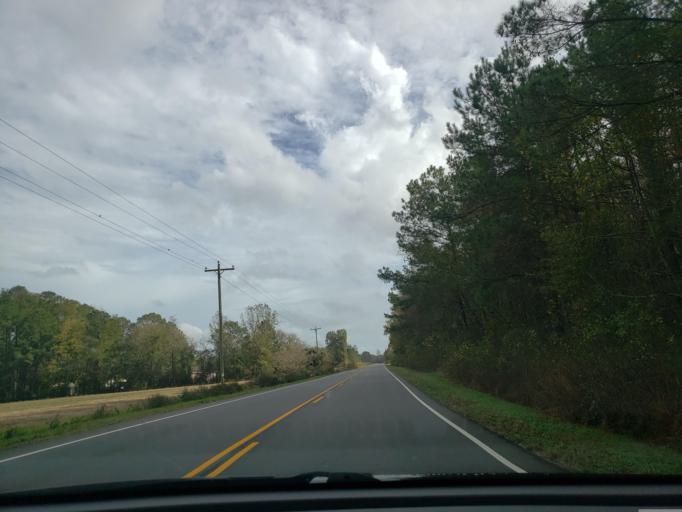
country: US
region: North Carolina
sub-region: Duplin County
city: Beulaville
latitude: 34.8297
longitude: -77.8480
